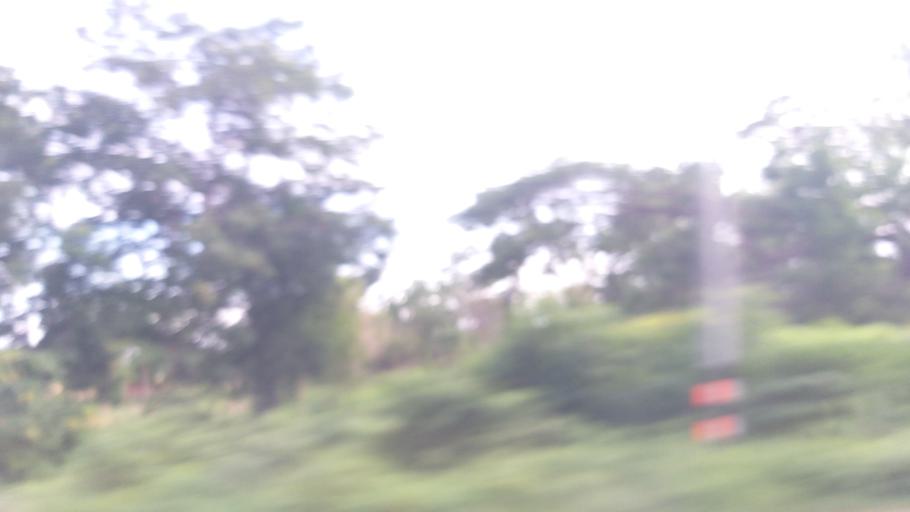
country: TH
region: Chaiyaphum
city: Phu Khiao
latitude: 16.3206
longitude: 102.2011
